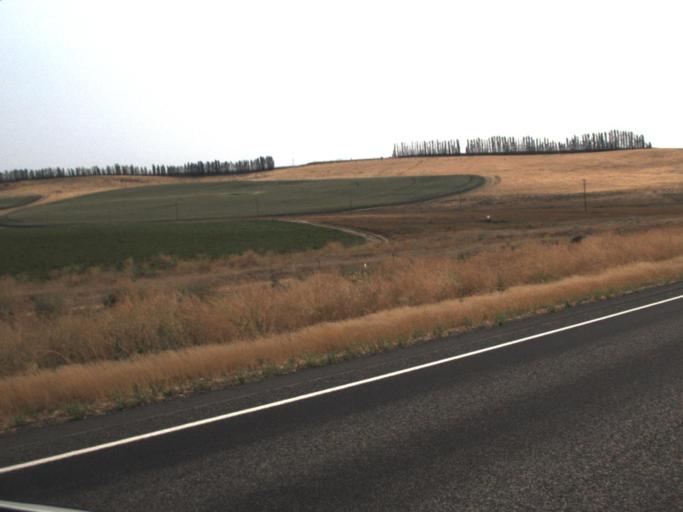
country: US
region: Oregon
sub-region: Morrow County
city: Irrigon
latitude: 45.9727
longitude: -119.6030
